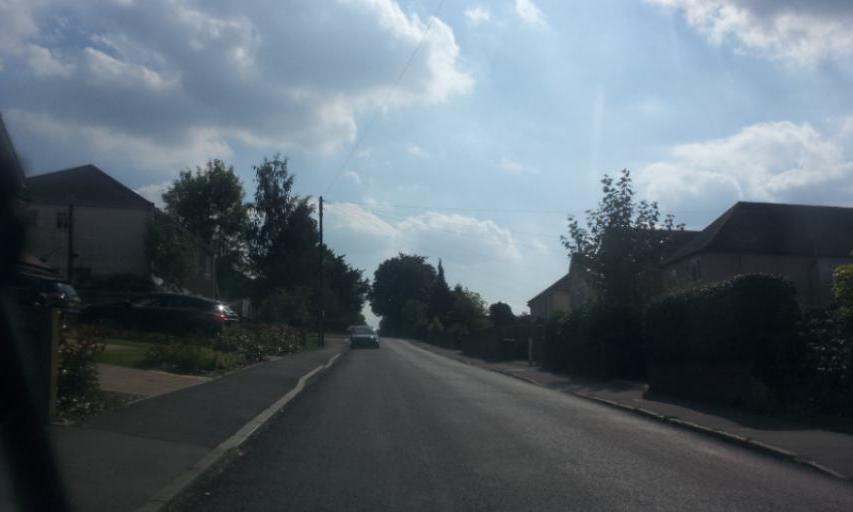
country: GB
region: England
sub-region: Kent
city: Maidstone
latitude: 51.2357
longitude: 0.4961
